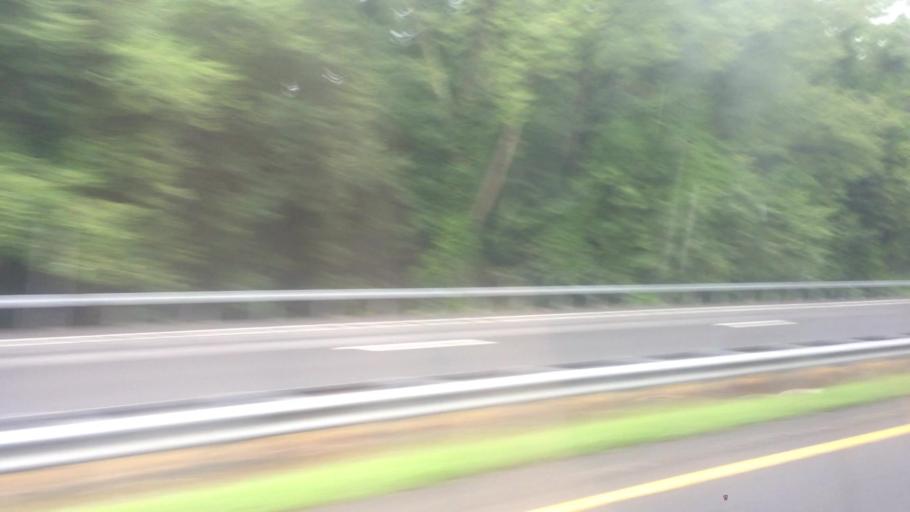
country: US
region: New York
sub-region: Ulster County
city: Kingston
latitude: 41.9400
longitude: -74.0209
